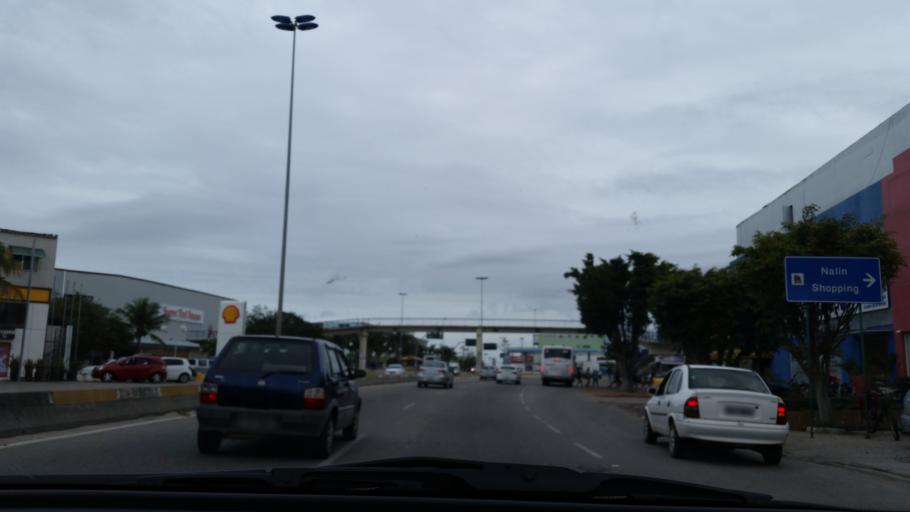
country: BR
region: Rio de Janeiro
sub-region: Sao Pedro Da Aldeia
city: Sao Pedro da Aldeia
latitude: -22.8345
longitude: -42.1001
